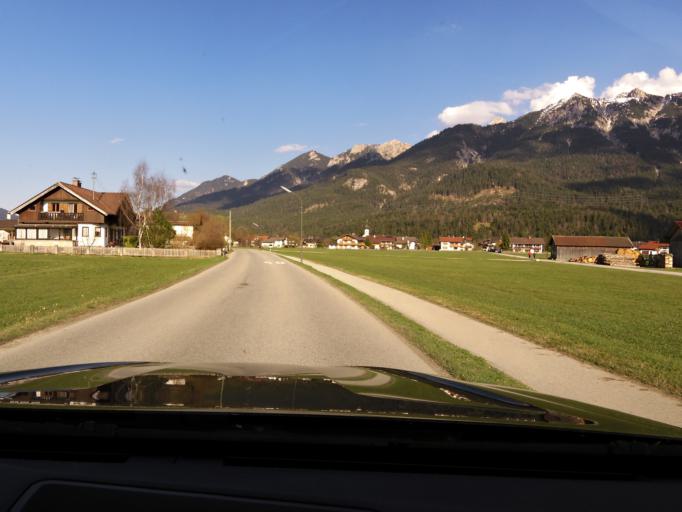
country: DE
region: Bavaria
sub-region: Upper Bavaria
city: Krun
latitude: 47.5038
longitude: 11.2721
